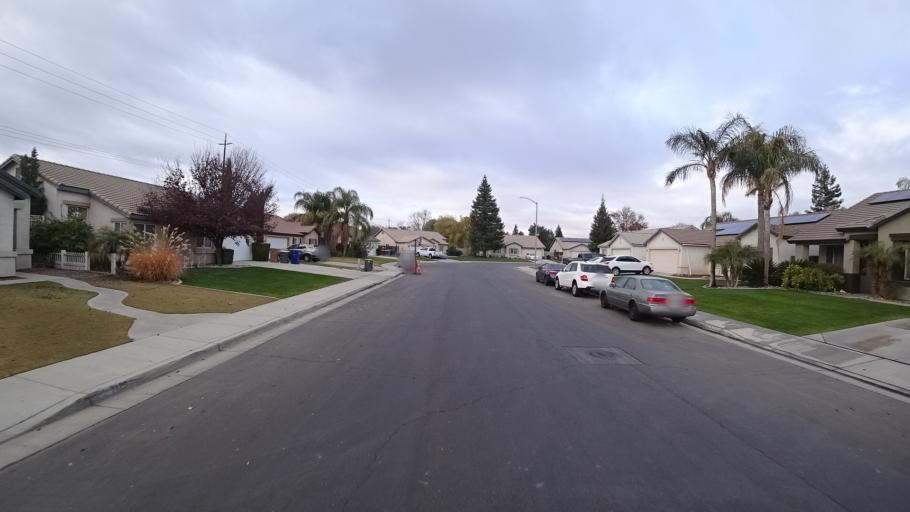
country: US
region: California
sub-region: Kern County
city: Greenfield
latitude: 35.2967
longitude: -119.0820
